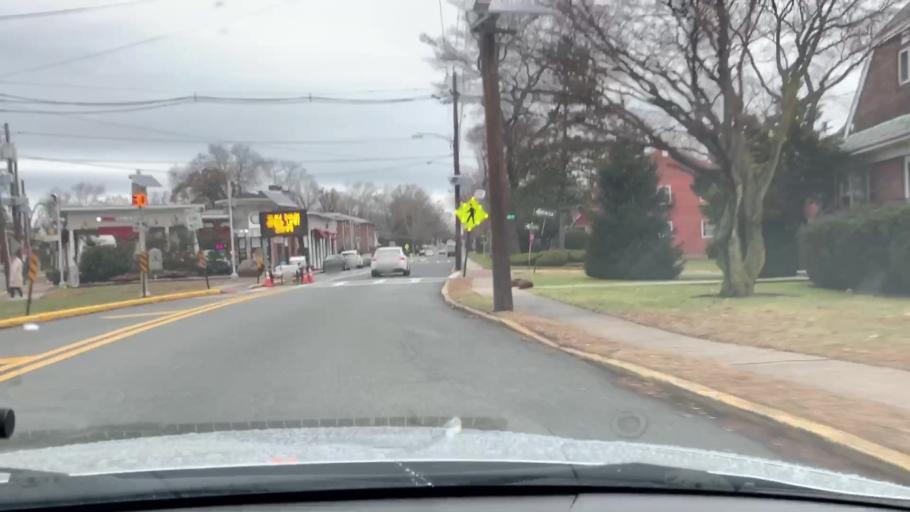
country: US
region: New Jersey
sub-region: Bergen County
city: Fort Lee
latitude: 40.8447
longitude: -73.9787
